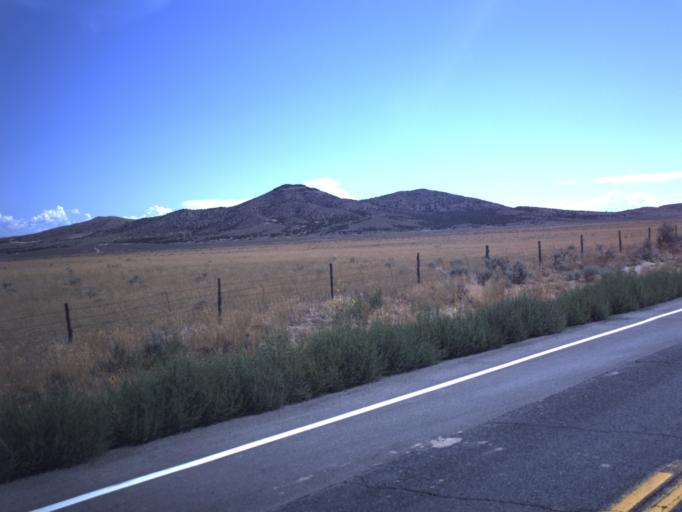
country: US
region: Utah
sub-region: Tooele County
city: Tooele
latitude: 40.0855
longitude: -112.4231
